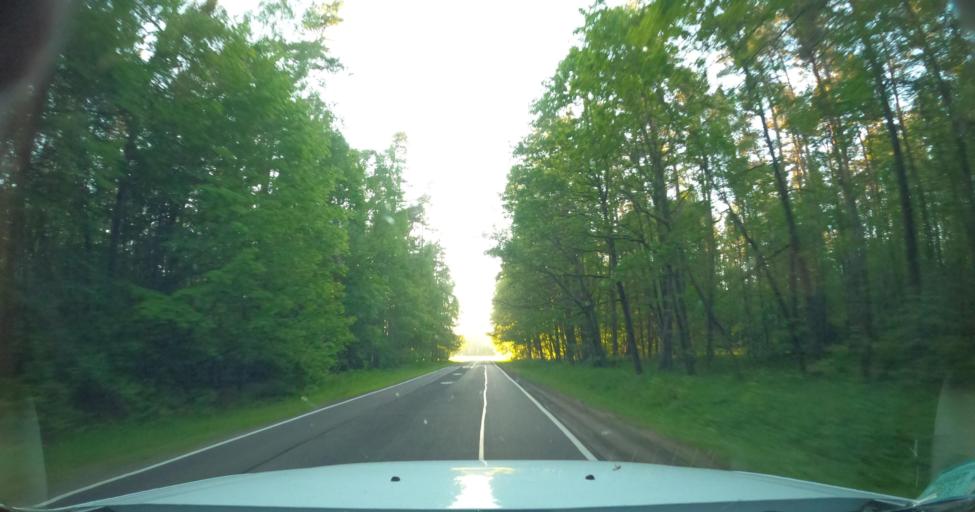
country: PL
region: Pomeranian Voivodeship
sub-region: Powiat bytowski
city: Czarna Dabrowka
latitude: 54.3836
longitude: 17.4844
